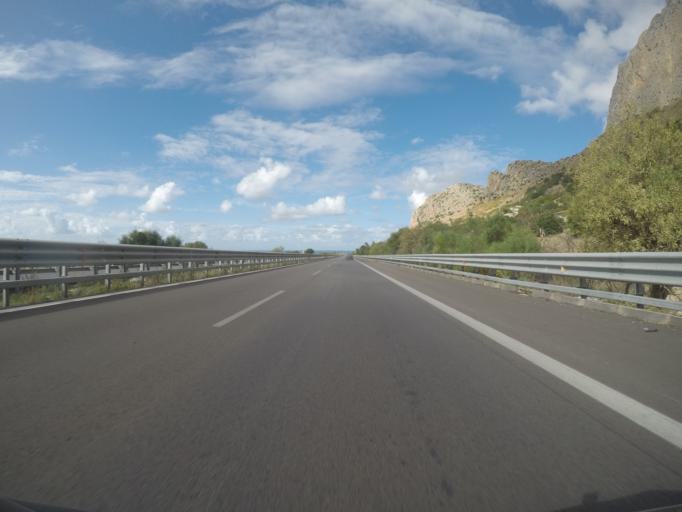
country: IT
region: Sicily
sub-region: Palermo
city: Cinisi
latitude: 38.1645
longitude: 13.1132
